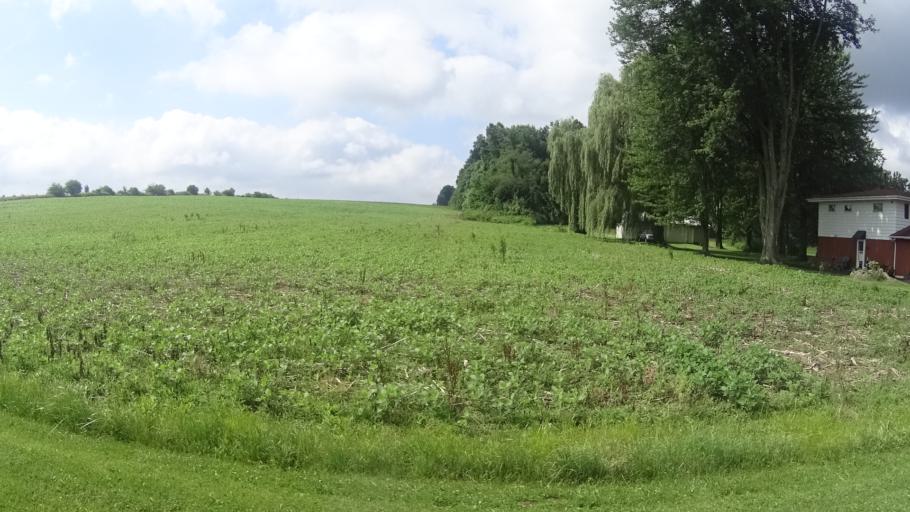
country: US
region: Ohio
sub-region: Huron County
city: Wakeman
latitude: 41.2955
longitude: -82.4486
